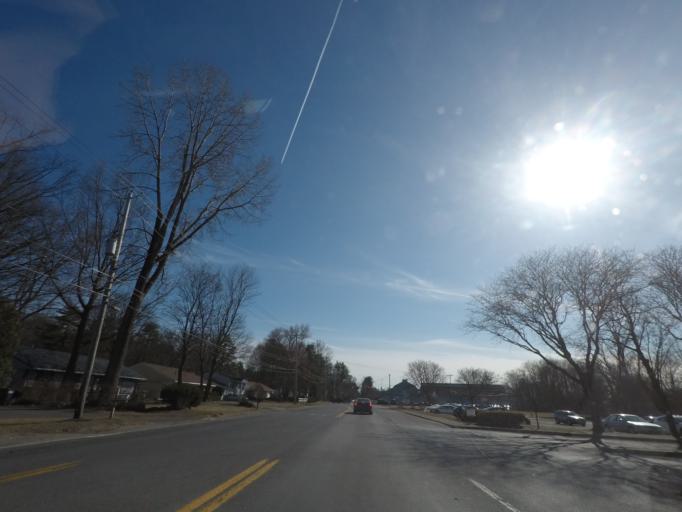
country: US
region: New York
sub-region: Saratoga County
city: Saratoga Springs
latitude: 43.0697
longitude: -73.7940
